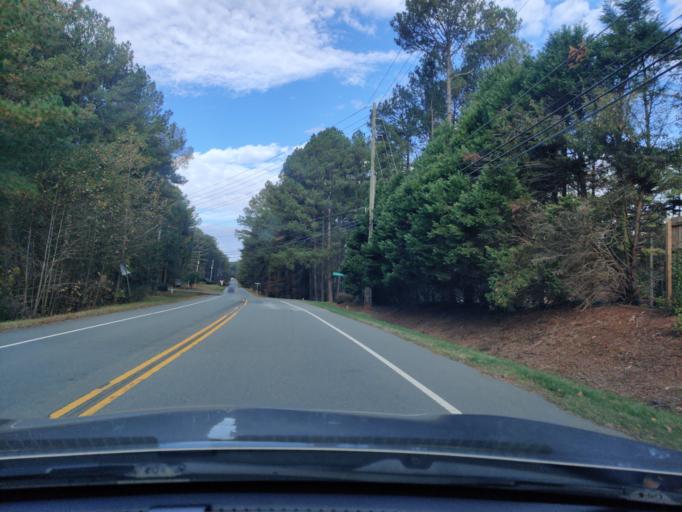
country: US
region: North Carolina
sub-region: Wake County
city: West Raleigh
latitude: 35.9171
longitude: -78.7115
